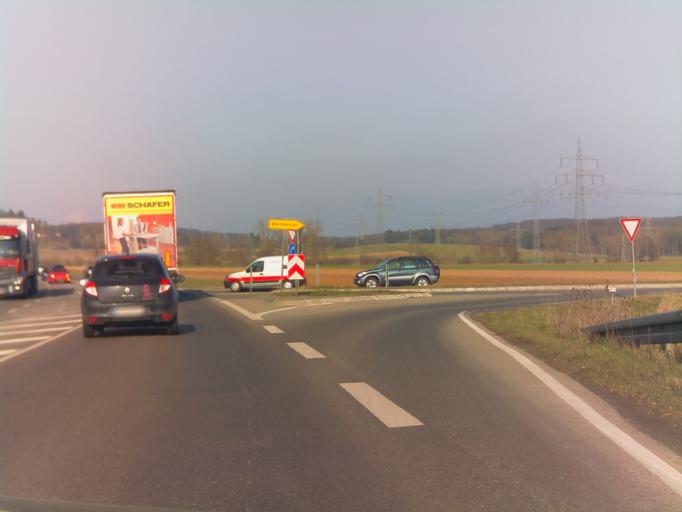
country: DE
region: Baden-Wuerttemberg
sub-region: Regierungsbezirk Stuttgart
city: Renningen
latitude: 48.7614
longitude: 8.9474
